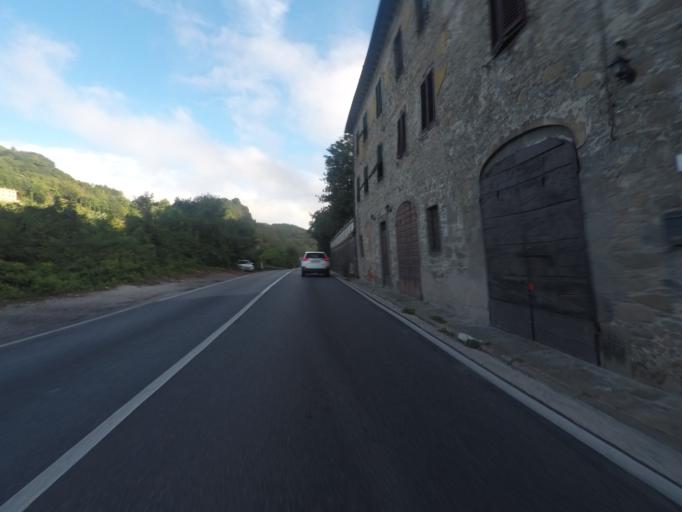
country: IT
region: Tuscany
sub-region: Provincia di Lucca
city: Borgo a Mozzano
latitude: 43.9836
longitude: 10.5530
